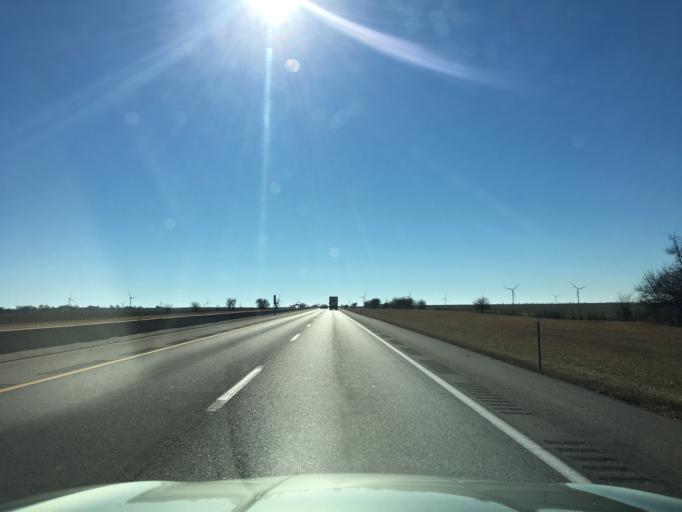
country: US
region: Kansas
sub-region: Sumner County
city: Wellington
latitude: 37.1822
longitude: -97.3396
